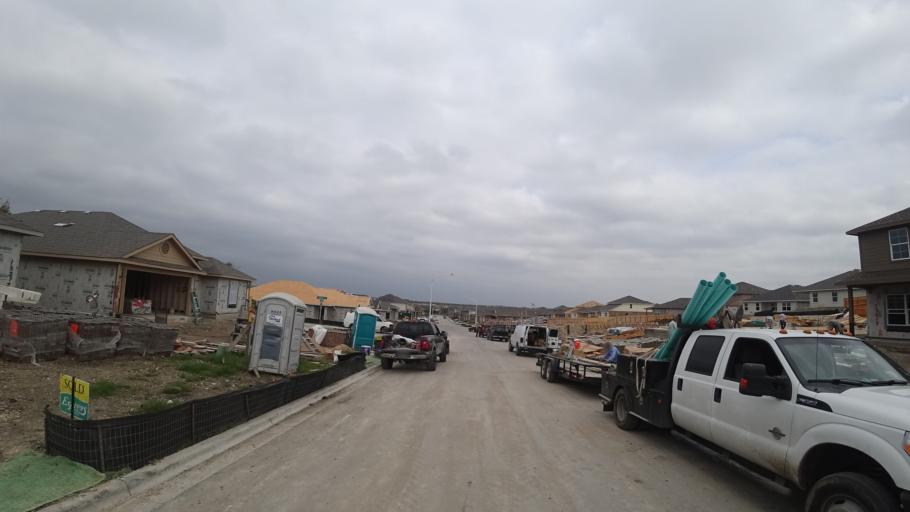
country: US
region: Texas
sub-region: Travis County
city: Pflugerville
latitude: 30.3920
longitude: -97.6225
